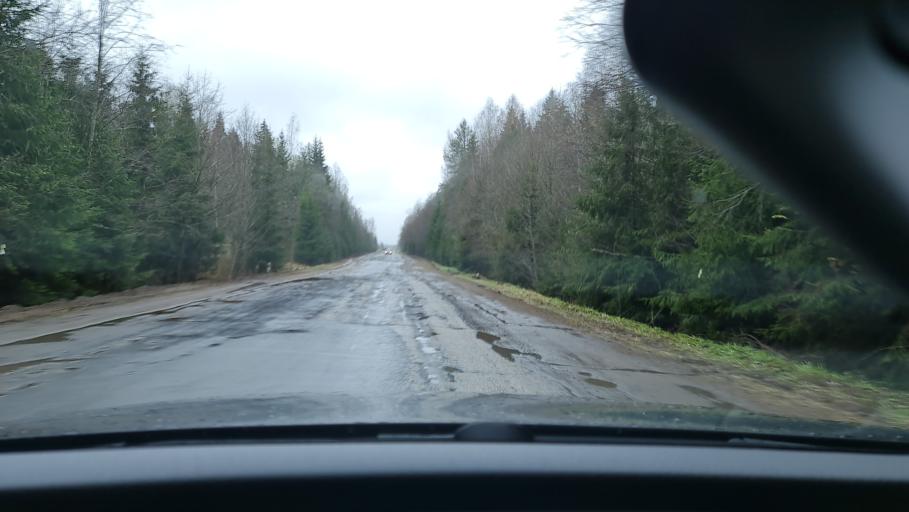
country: RU
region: Novgorod
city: Valday
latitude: 58.0352
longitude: 32.8607
